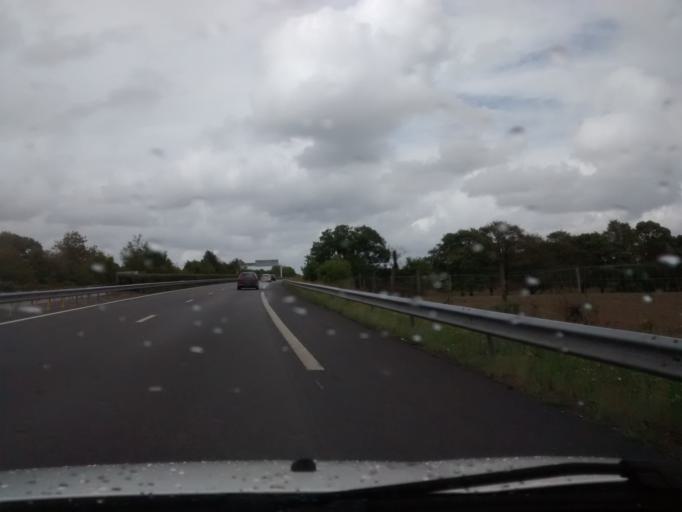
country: FR
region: Brittany
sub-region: Departement du Morbihan
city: Trefflean
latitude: 47.7081
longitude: -2.6165
